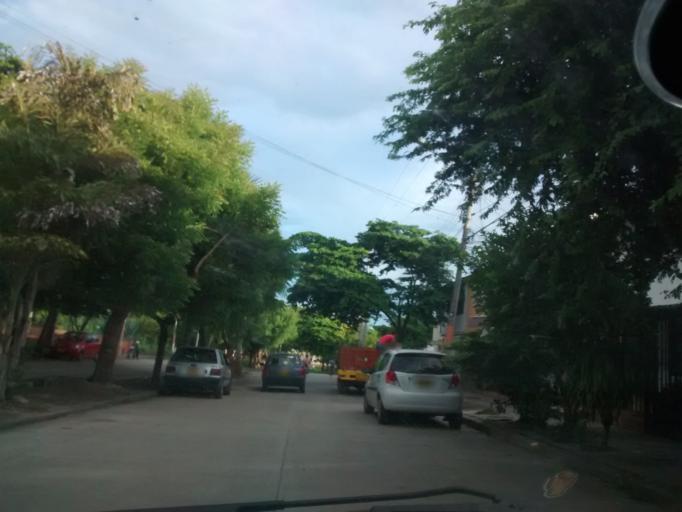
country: CO
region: Cundinamarca
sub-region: Girardot
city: Girardot City
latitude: 4.3094
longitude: -74.7992
